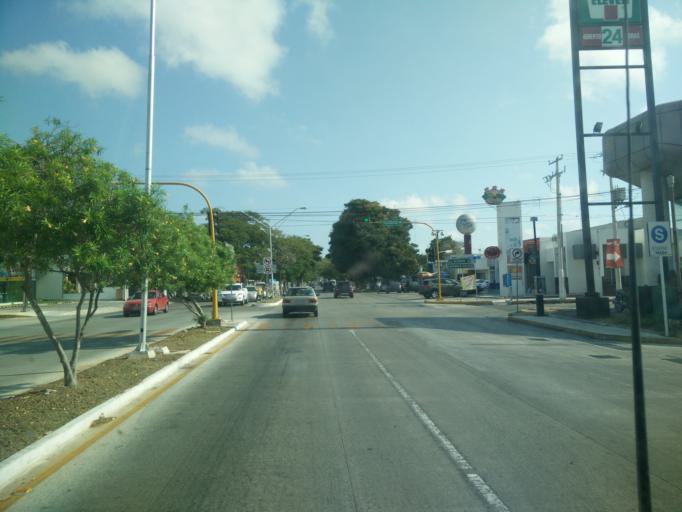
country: MX
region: Yucatan
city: Merida
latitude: 21.0035
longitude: -89.6150
